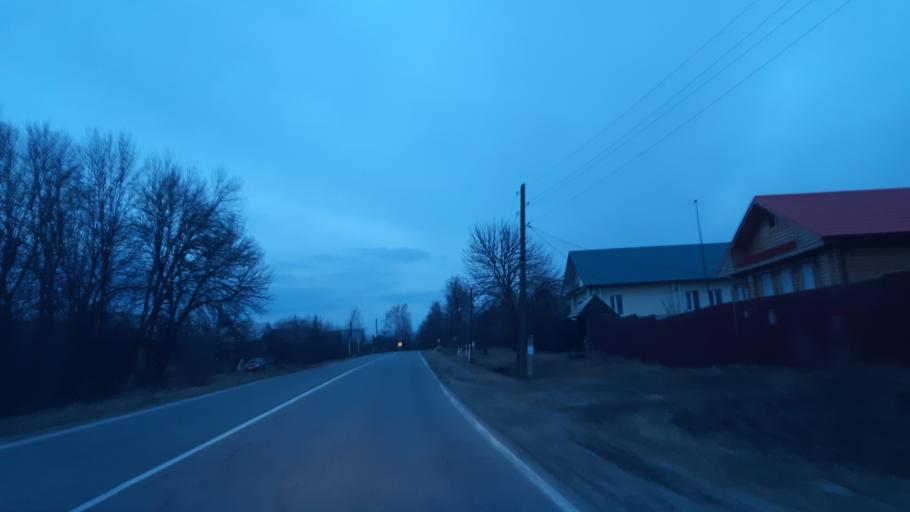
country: RU
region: Vladimir
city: Luknovo
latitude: 56.1871
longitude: 42.0190
